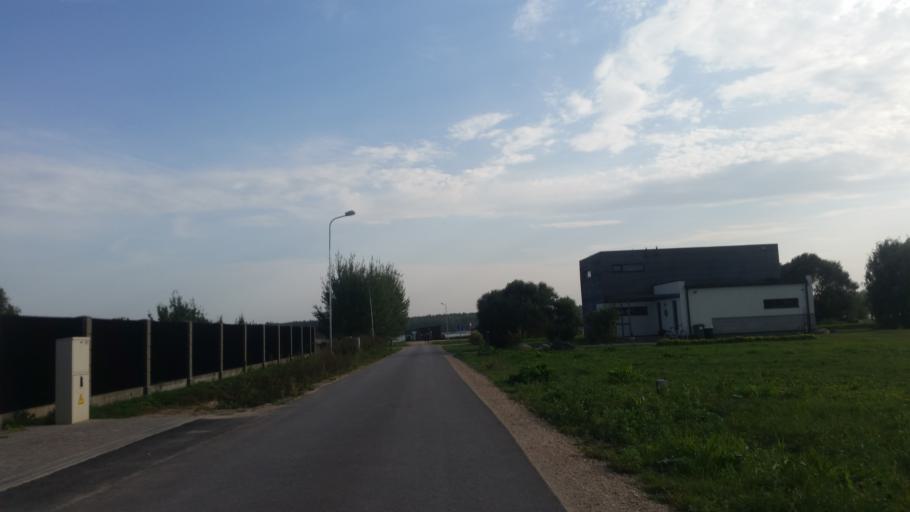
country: LV
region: Ikskile
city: Ikskile
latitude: 56.8178
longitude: 24.5114
